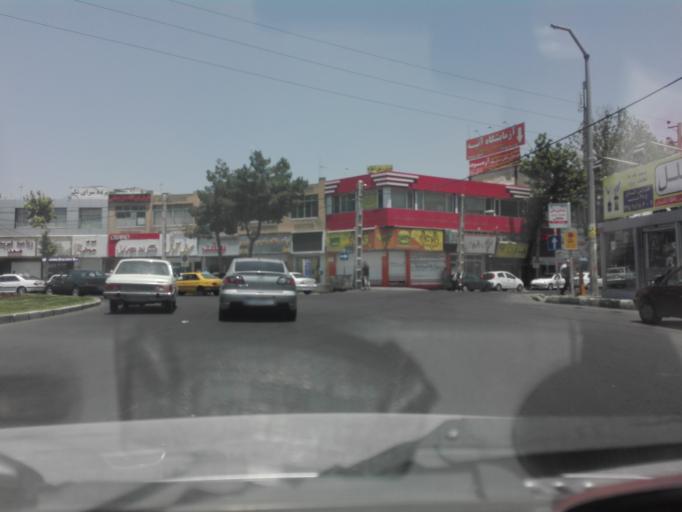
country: IR
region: Tehran
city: Shahre Jadide Andisheh
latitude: 35.7199
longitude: 50.9873
